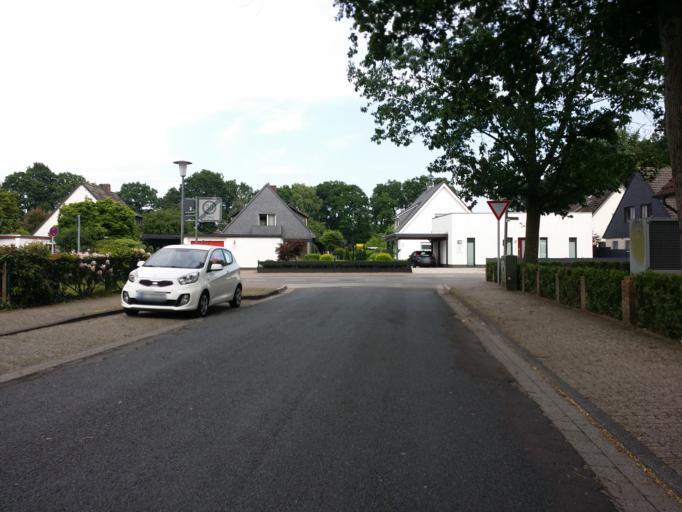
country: DE
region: Lower Saxony
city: Oldenburg
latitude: 53.1473
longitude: 8.2415
